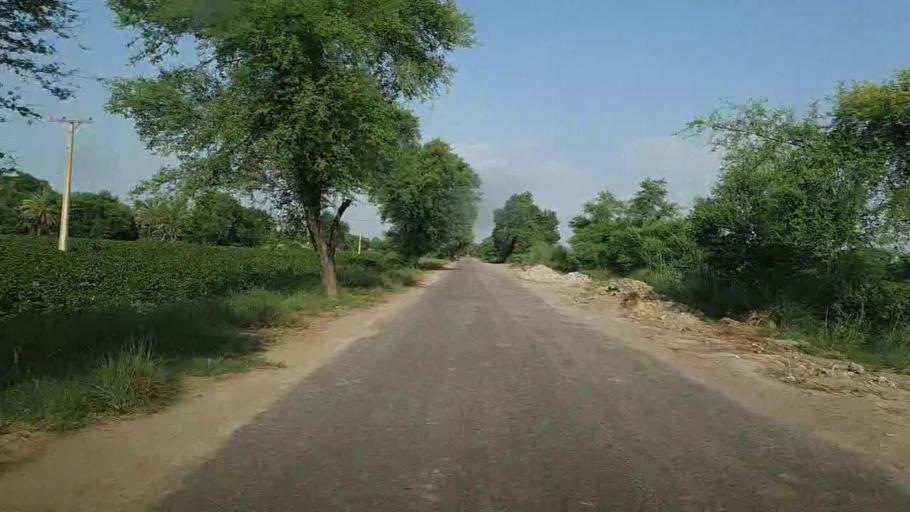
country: PK
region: Sindh
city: Khairpur
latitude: 28.0751
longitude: 69.8158
